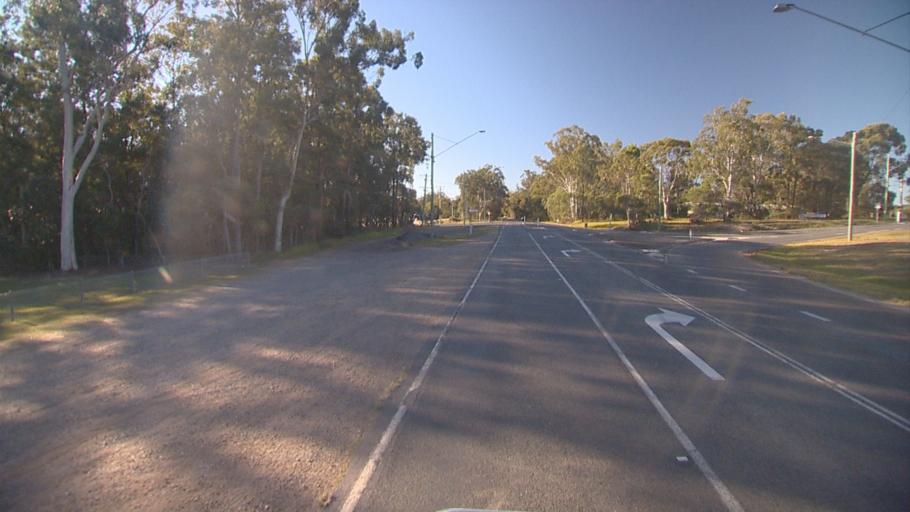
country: AU
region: Queensland
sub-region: Logan
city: Logan Reserve
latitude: -27.7353
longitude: 153.0881
